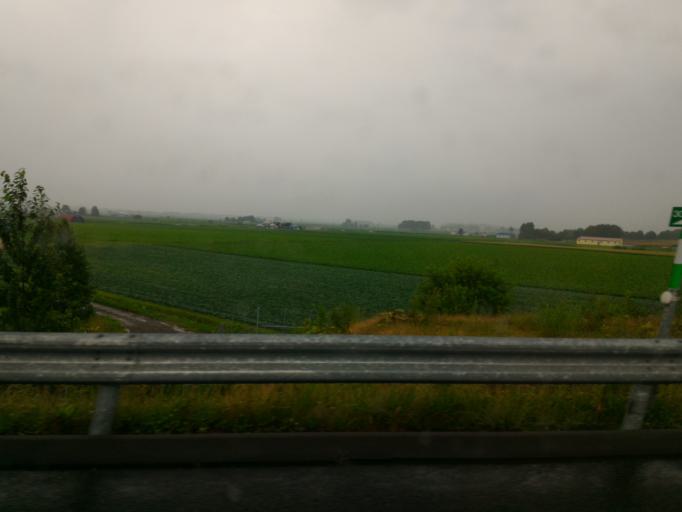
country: JP
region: Hokkaido
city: Nayoro
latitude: 44.4340
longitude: 142.3727
